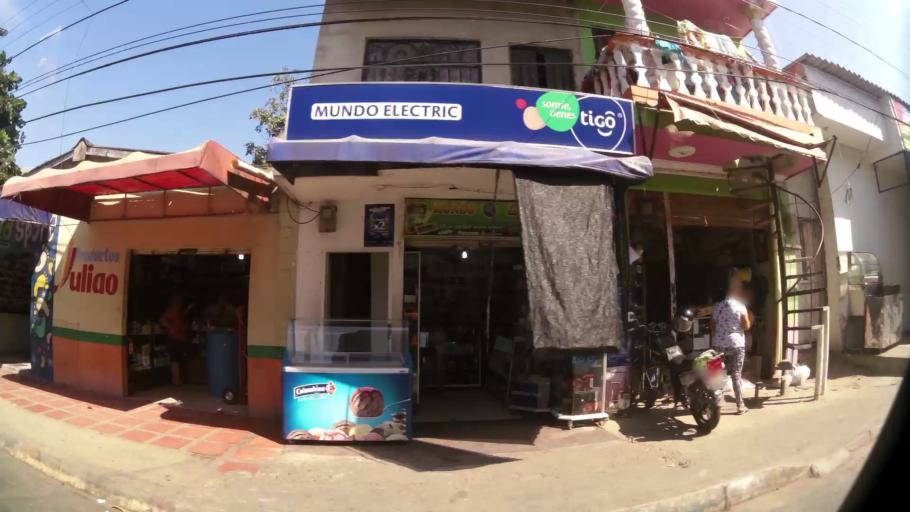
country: CO
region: Atlantico
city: Barranquilla
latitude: 10.9351
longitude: -74.8252
